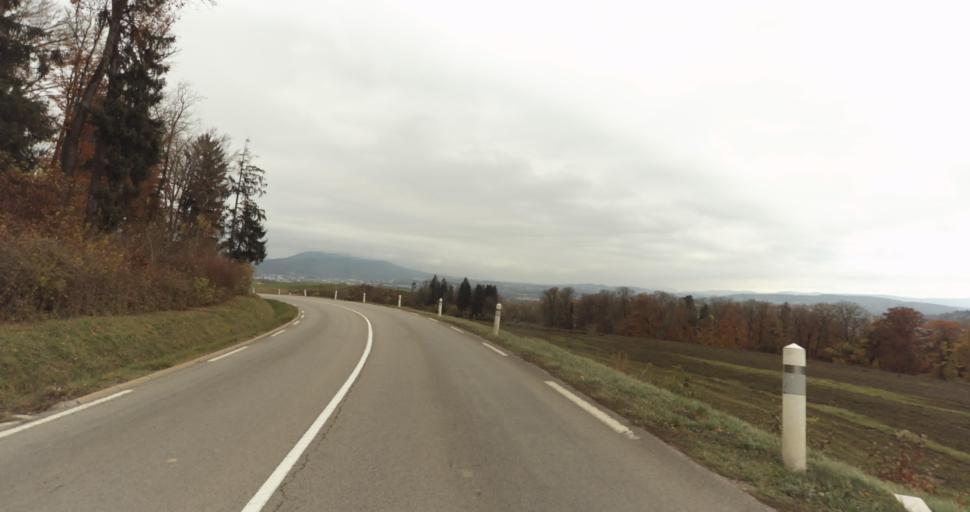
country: FR
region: Rhone-Alpes
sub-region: Departement de la Haute-Savoie
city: Pringy
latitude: 45.9584
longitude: 6.1257
